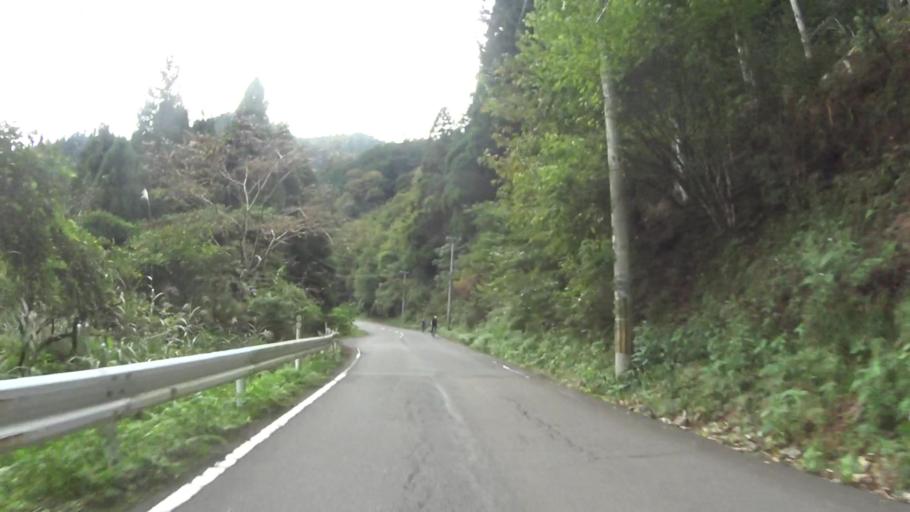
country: JP
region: Fukui
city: Obama
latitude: 35.3178
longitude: 135.6506
